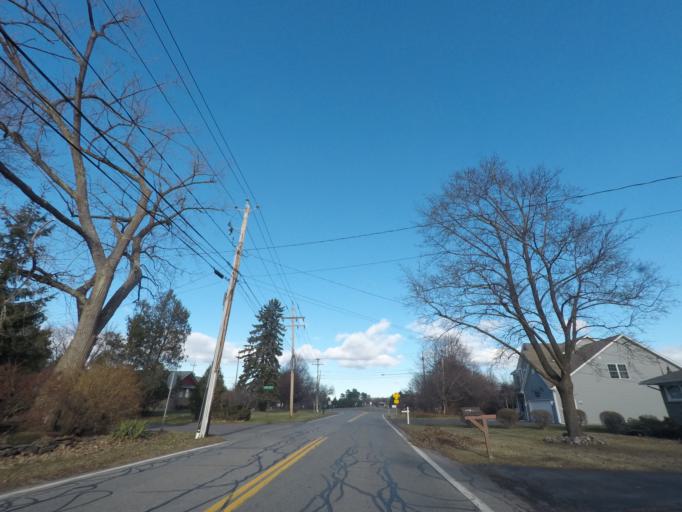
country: US
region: New York
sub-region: Schenectady County
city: Niskayuna
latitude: 42.8239
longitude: -73.8798
